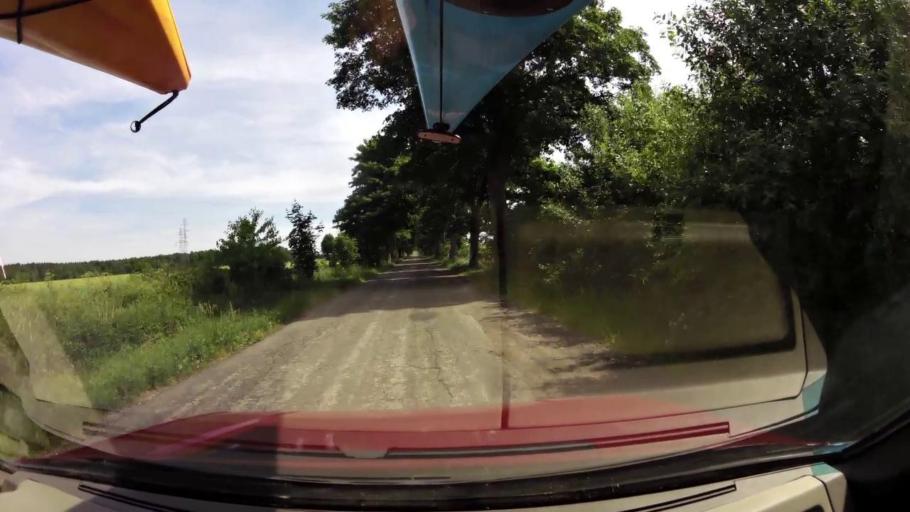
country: PL
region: West Pomeranian Voivodeship
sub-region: Powiat koszalinski
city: Sianow
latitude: 54.3197
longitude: 16.3284
